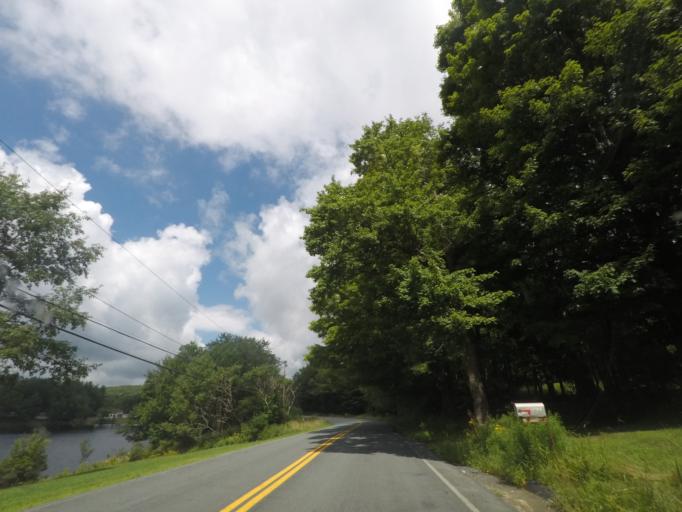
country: US
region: New York
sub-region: Rensselaer County
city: Averill Park
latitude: 42.6444
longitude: -73.4809
